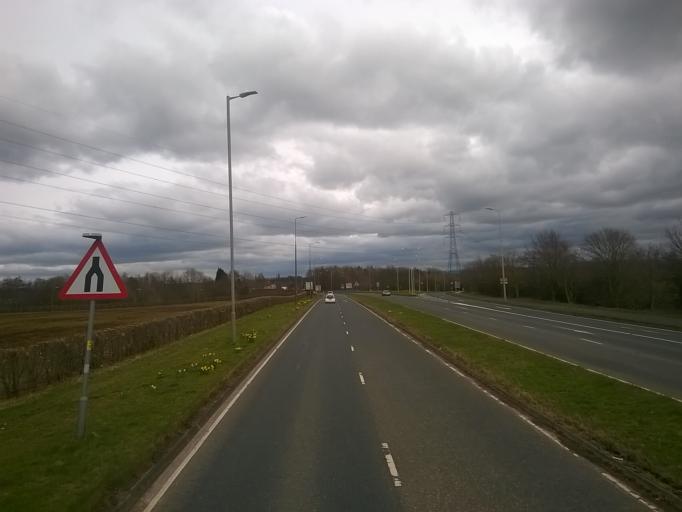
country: GB
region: England
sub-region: Lancashire
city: Preston
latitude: 53.7641
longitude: -2.7787
